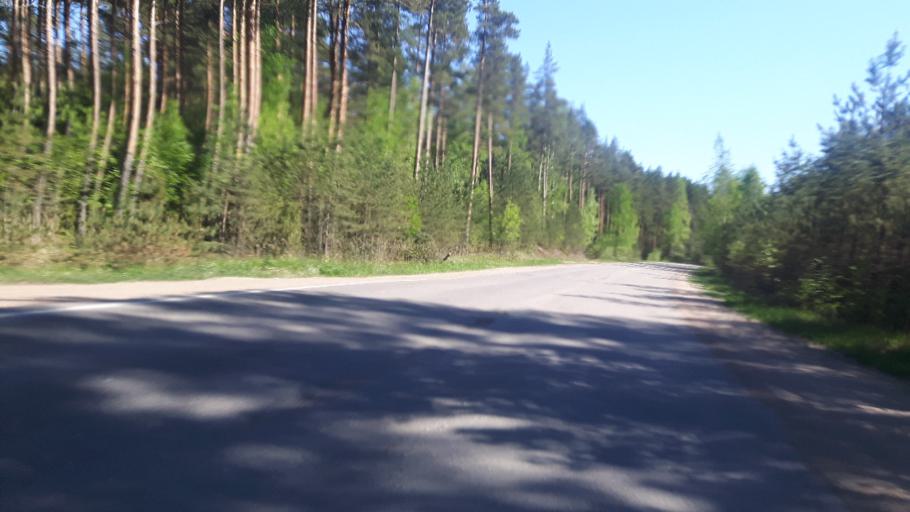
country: RU
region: Leningrad
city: Glebychevo
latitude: 60.2412
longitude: 29.0016
